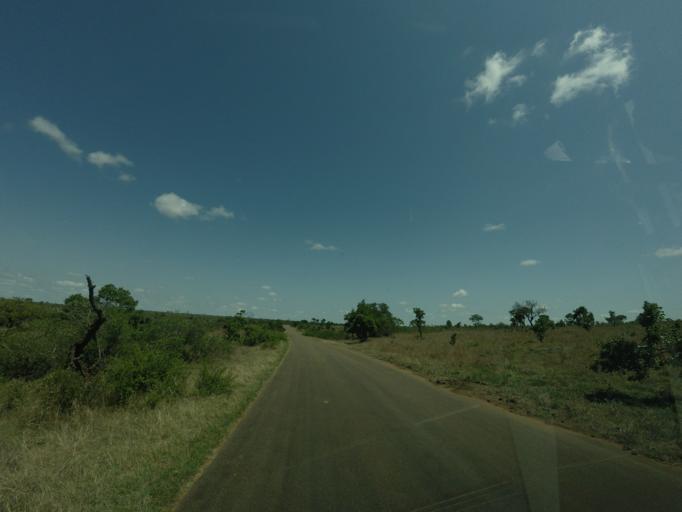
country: ZA
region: Mpumalanga
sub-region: Ehlanzeni District
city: Komatipoort
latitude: -24.9944
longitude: 31.9099
